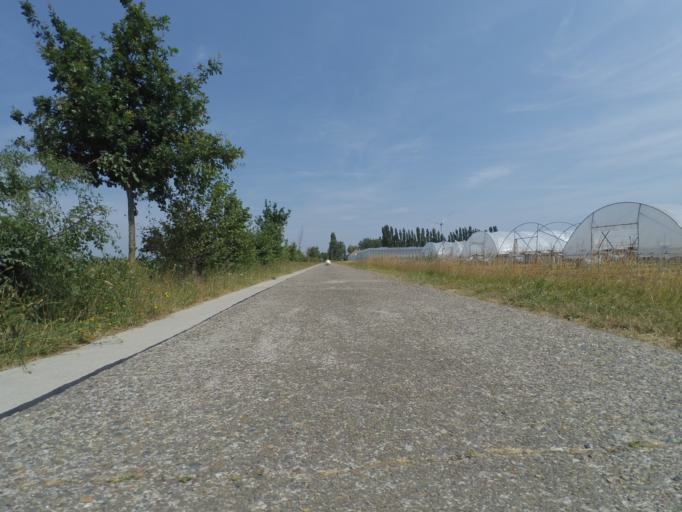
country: NL
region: North Brabant
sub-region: Gemeente Zundert
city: Zundert
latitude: 51.4123
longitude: 4.6904
